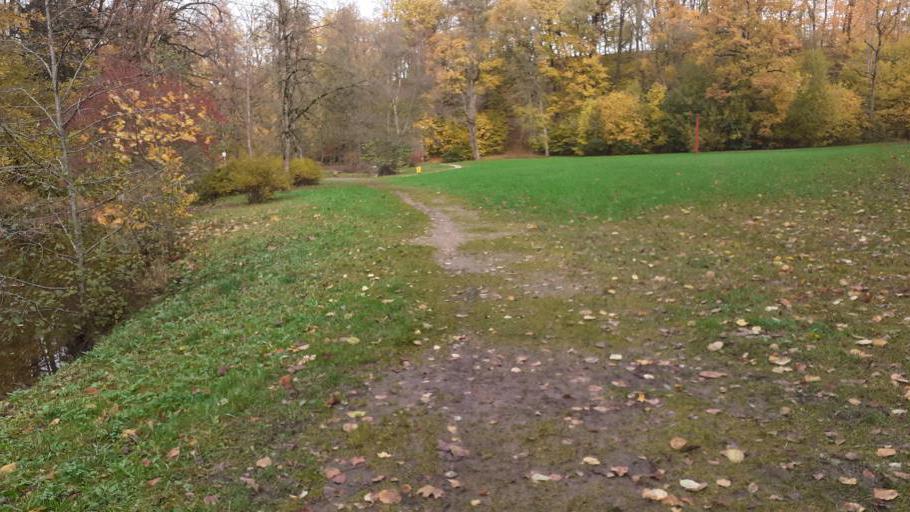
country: LV
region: Saldus Rajons
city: Saldus
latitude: 56.6667
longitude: 22.5166
